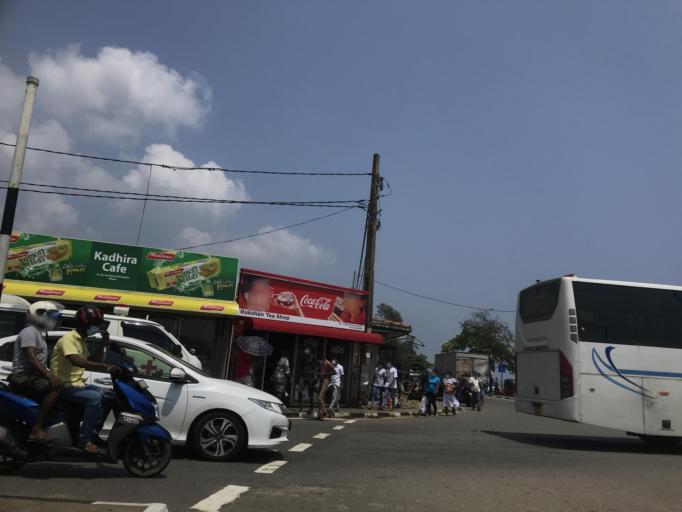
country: LK
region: Southern
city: Matara
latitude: 5.9433
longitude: 80.5496
